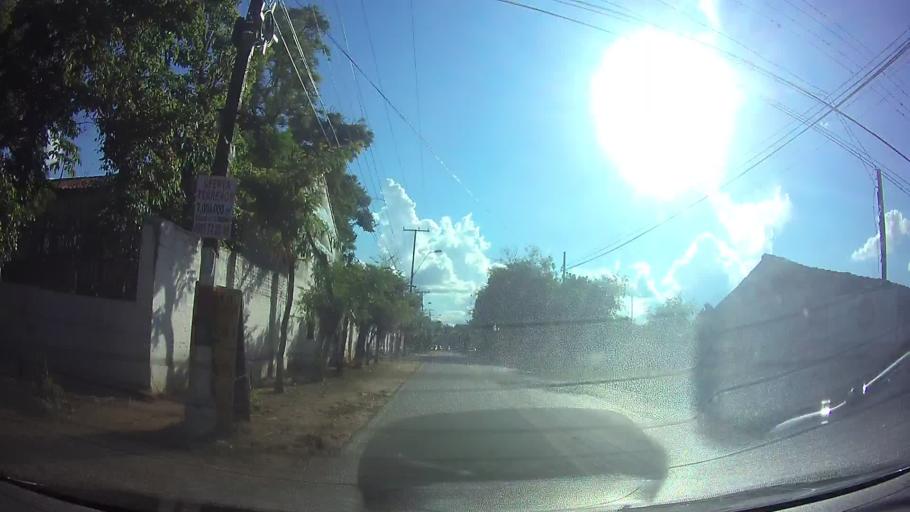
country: PY
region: Central
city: Aregua
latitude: -25.3143
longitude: -57.3859
